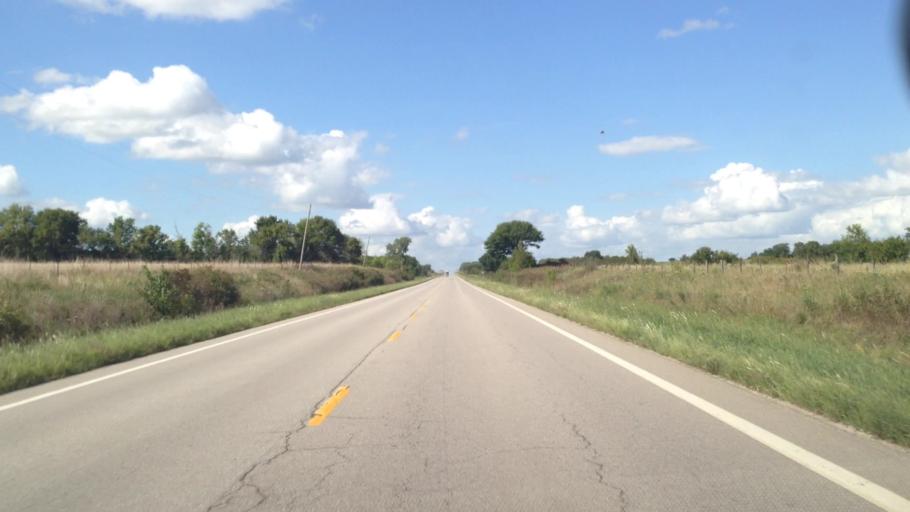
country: US
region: Kansas
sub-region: Neosho County
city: Erie
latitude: 37.7101
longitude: -95.1607
